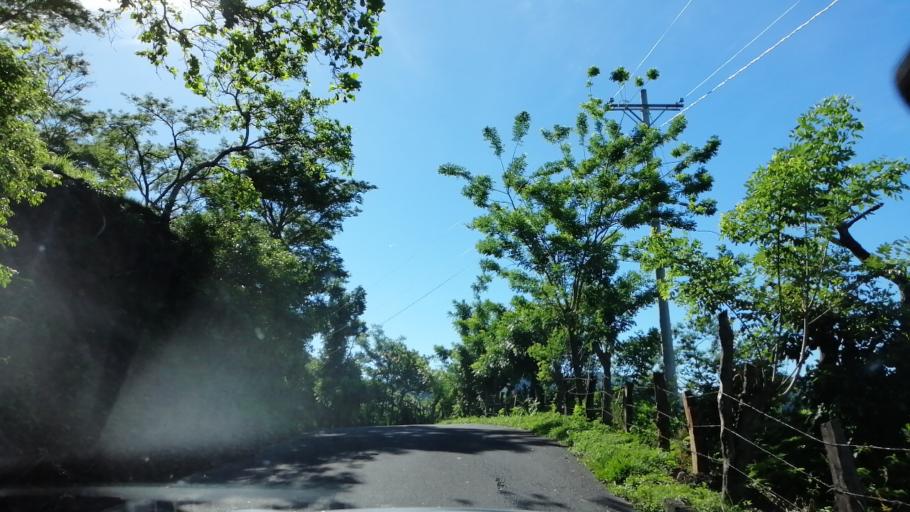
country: SV
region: Morazan
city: Corinto
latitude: 13.7901
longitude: -88.0229
